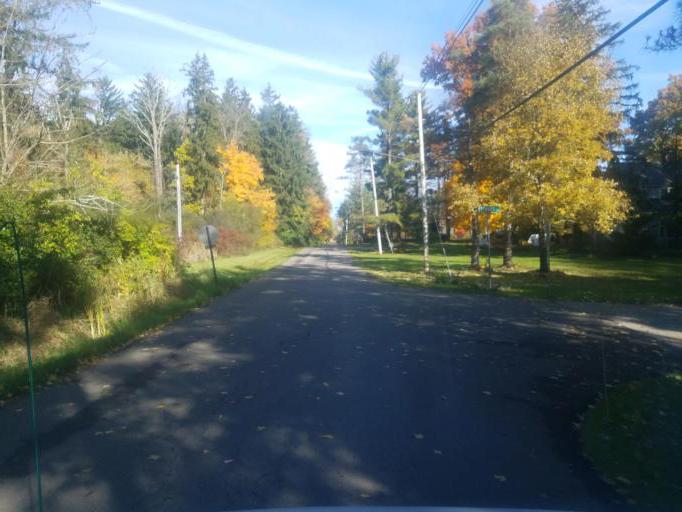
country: US
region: Ohio
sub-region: Richland County
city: Mansfield
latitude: 40.7367
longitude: -82.5422
